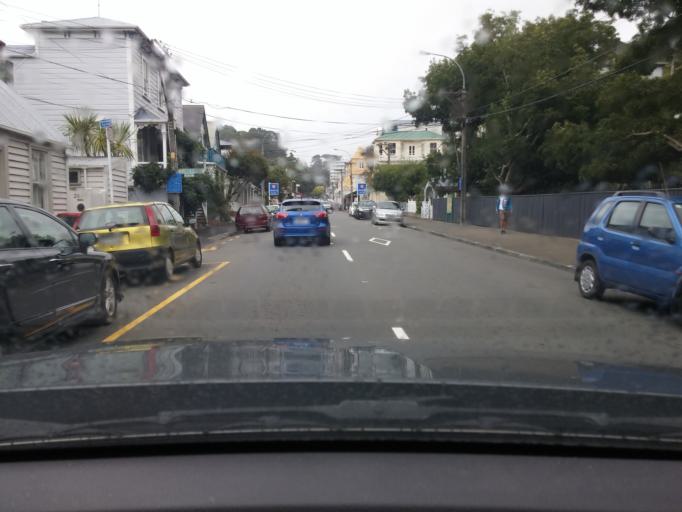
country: NZ
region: Wellington
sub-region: Wellington City
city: Kelburn
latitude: -41.2771
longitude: 174.7712
